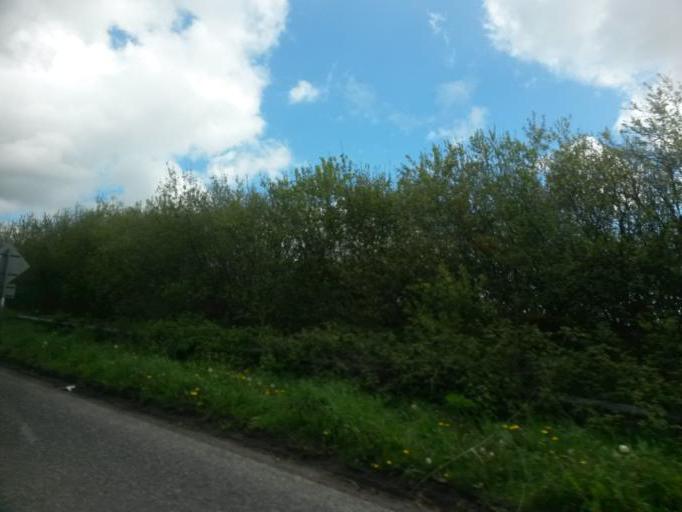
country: IE
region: Leinster
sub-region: Loch Garman
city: Castlebridge
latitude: 52.3790
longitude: -6.5198
